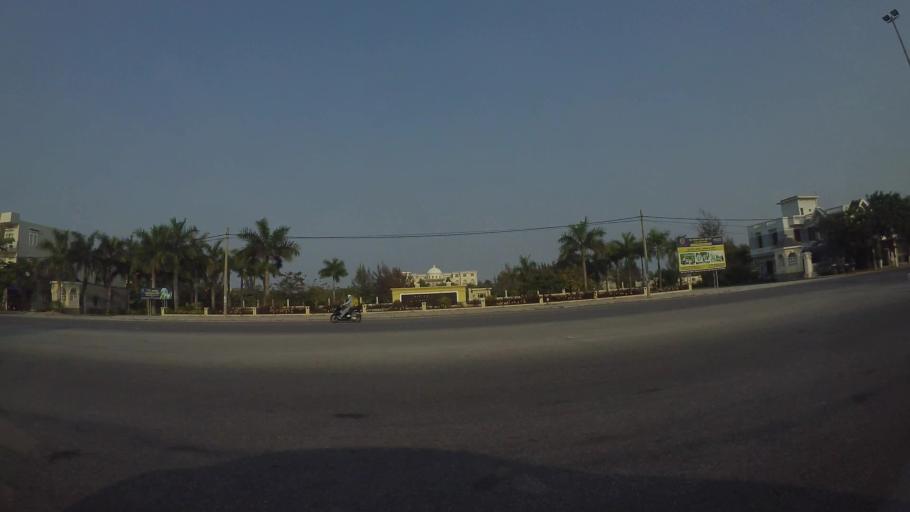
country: VN
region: Da Nang
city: Ngu Hanh Son
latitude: 15.9738
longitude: 108.2546
